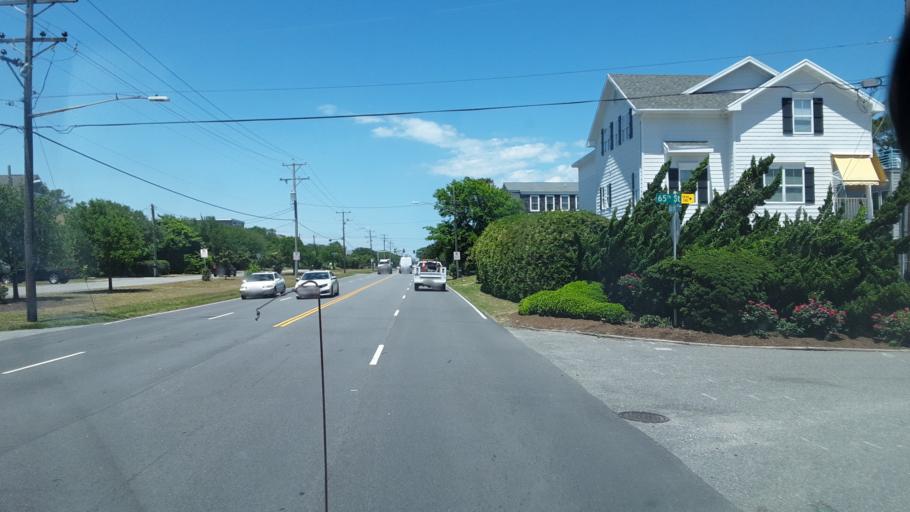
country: US
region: Virginia
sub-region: City of Virginia Beach
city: Virginia Beach
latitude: 36.8903
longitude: -75.9883
